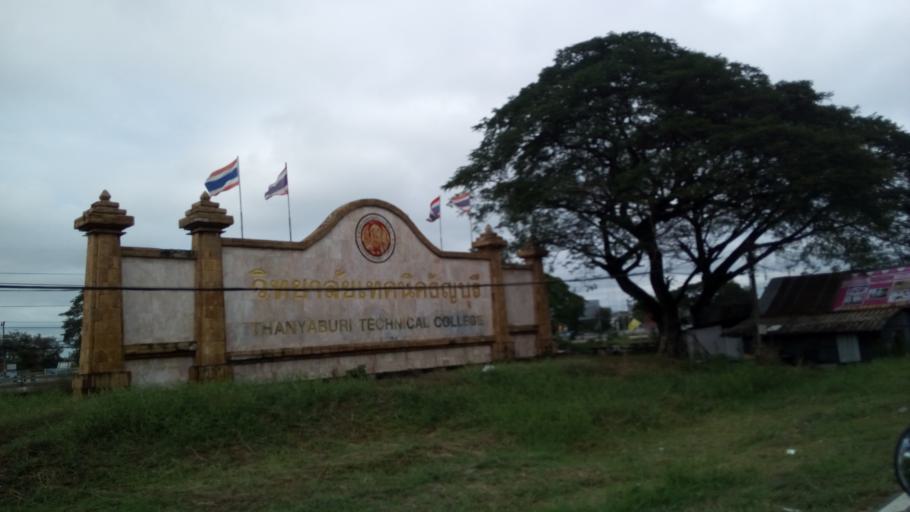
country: TH
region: Pathum Thani
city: Nong Suea
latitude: 14.0741
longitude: 100.8880
